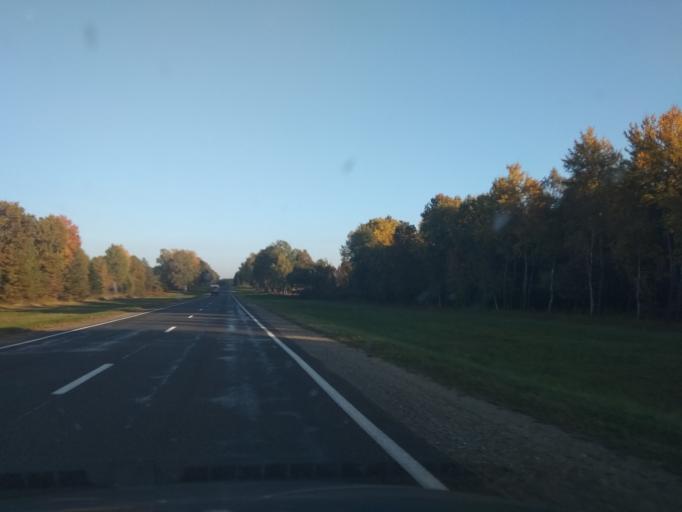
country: BY
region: Grodnenskaya
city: Vawkavysk
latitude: 53.1444
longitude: 24.6146
